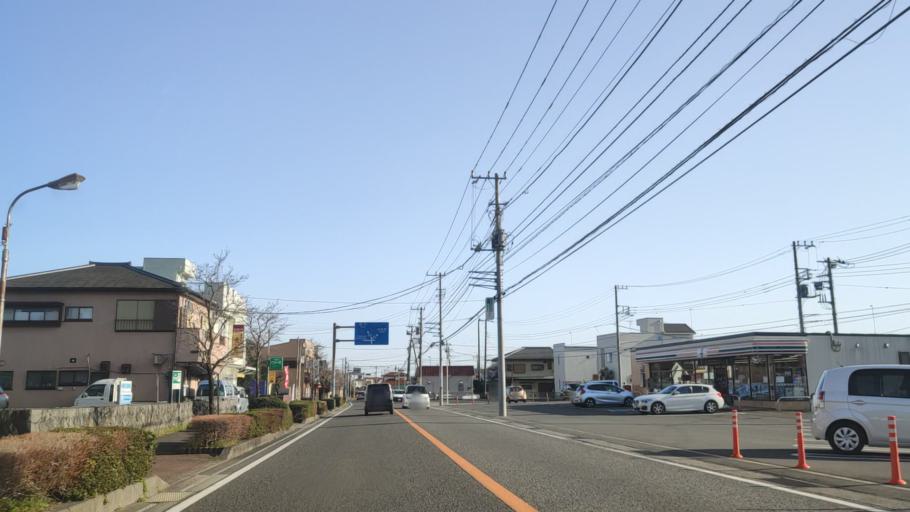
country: JP
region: Kanagawa
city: Zama
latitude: 35.5076
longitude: 139.3398
